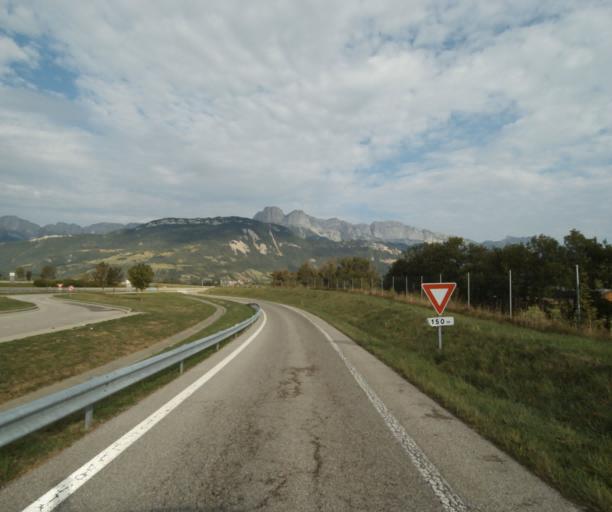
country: FR
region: Rhone-Alpes
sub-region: Departement de l'Isere
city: Le Gua
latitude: 44.9623
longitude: 5.6490
